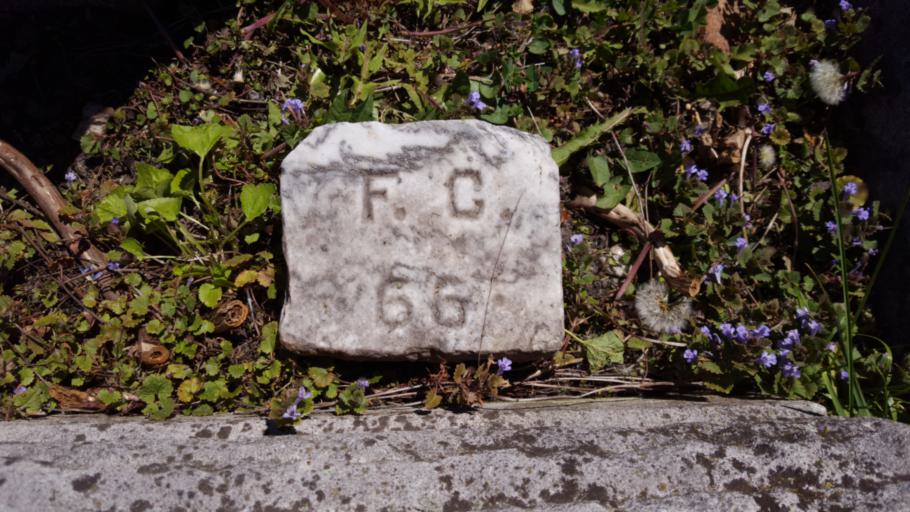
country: US
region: Illinois
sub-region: Cook County
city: Northbrook
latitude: 42.1024
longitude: -87.8281
